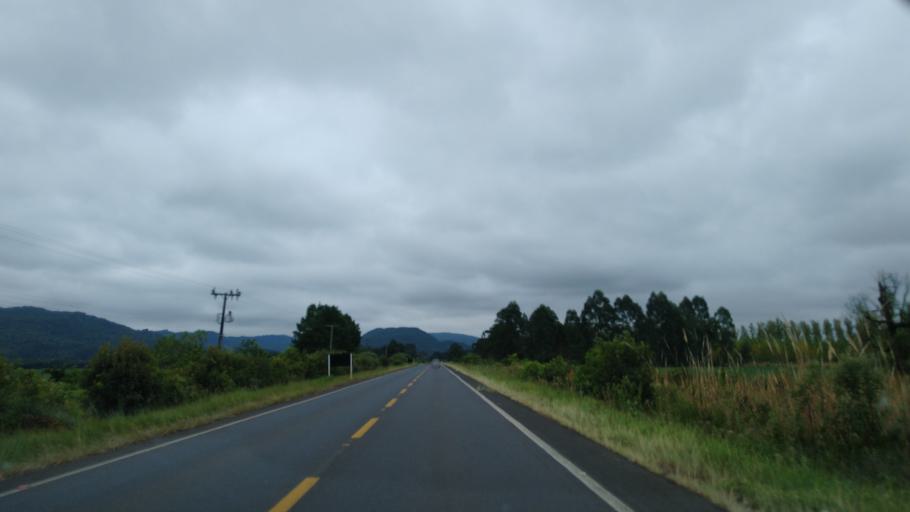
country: BR
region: Santa Catarina
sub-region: Porto Uniao
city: Porto Uniao
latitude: -26.2846
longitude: -51.0231
